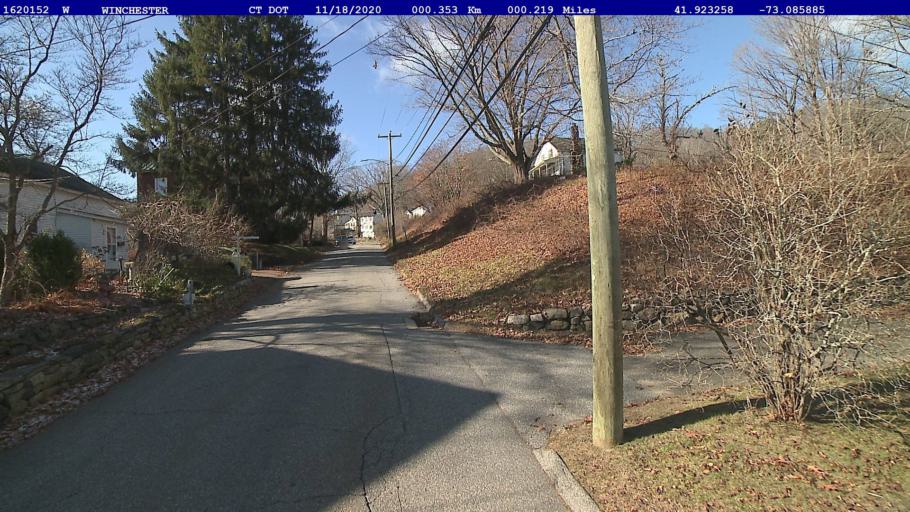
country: US
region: Connecticut
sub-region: Litchfield County
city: Winsted
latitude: 41.9233
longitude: -73.0859
